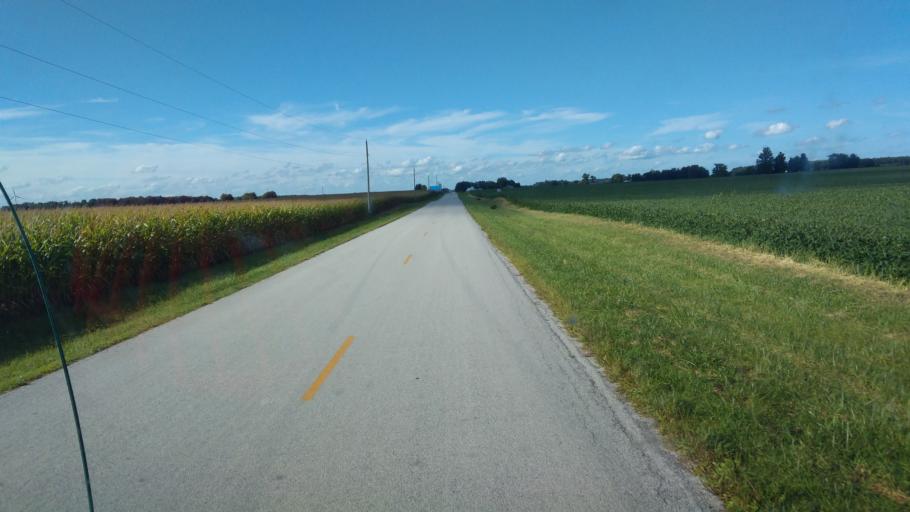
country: US
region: Ohio
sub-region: Hardin County
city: Kenton
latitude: 40.7355
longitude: -83.6908
